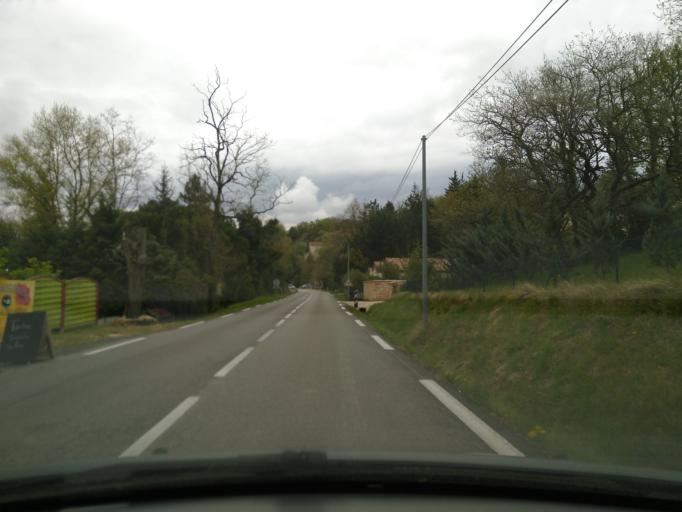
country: FR
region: Rhone-Alpes
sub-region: Departement de l'Ardeche
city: Ruoms
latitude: 44.3858
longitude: 4.3767
